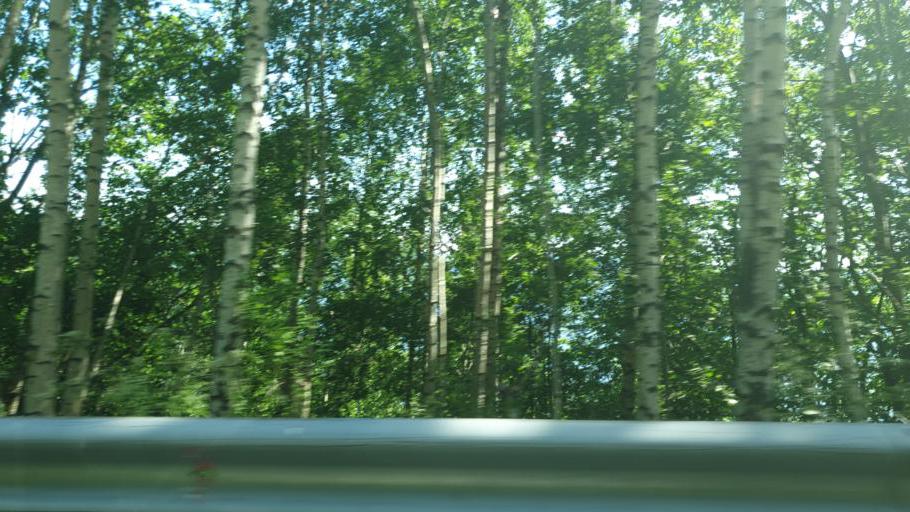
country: NO
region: Nord-Trondelag
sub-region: Frosta
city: Frosta
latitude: 63.7071
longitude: 10.7613
